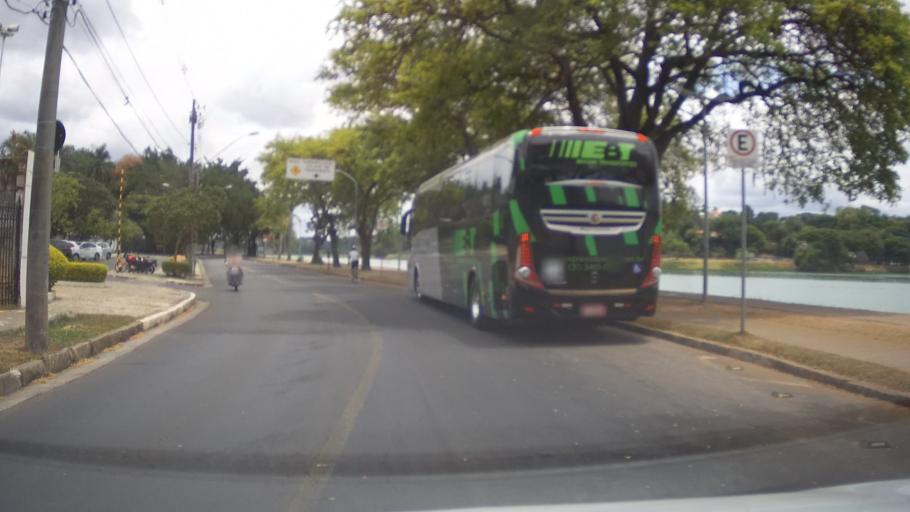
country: BR
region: Minas Gerais
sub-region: Belo Horizonte
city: Belo Horizonte
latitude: -19.8545
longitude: -43.9802
